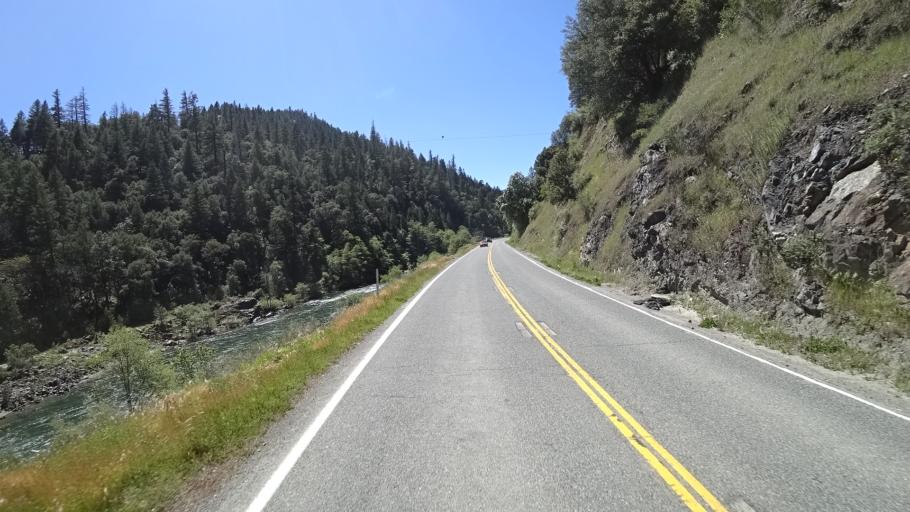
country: US
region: California
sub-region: Trinity County
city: Hayfork
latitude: 40.7784
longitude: -123.3133
